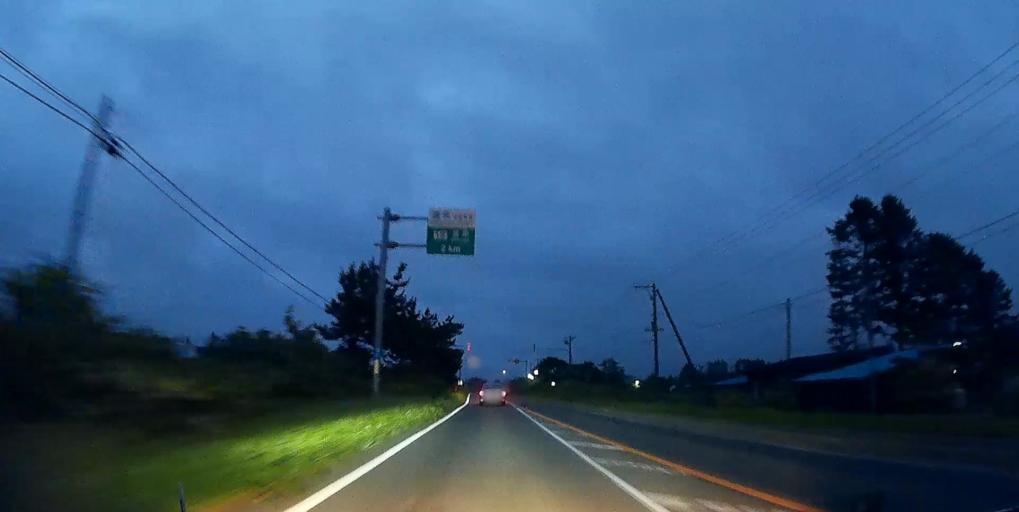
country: JP
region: Hokkaido
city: Nanae
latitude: 42.2183
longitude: 140.3807
